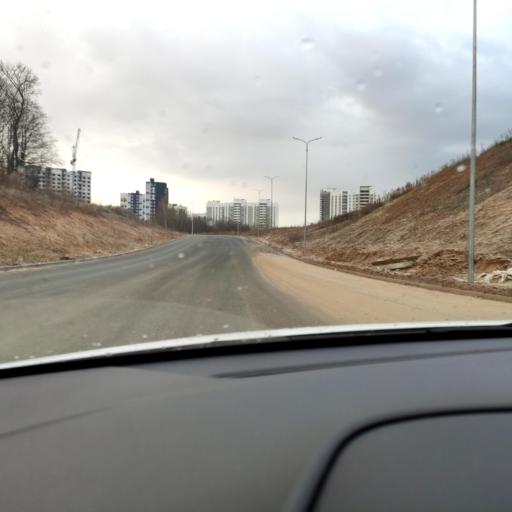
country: RU
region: Tatarstan
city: Osinovo
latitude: 55.8634
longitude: 48.9015
